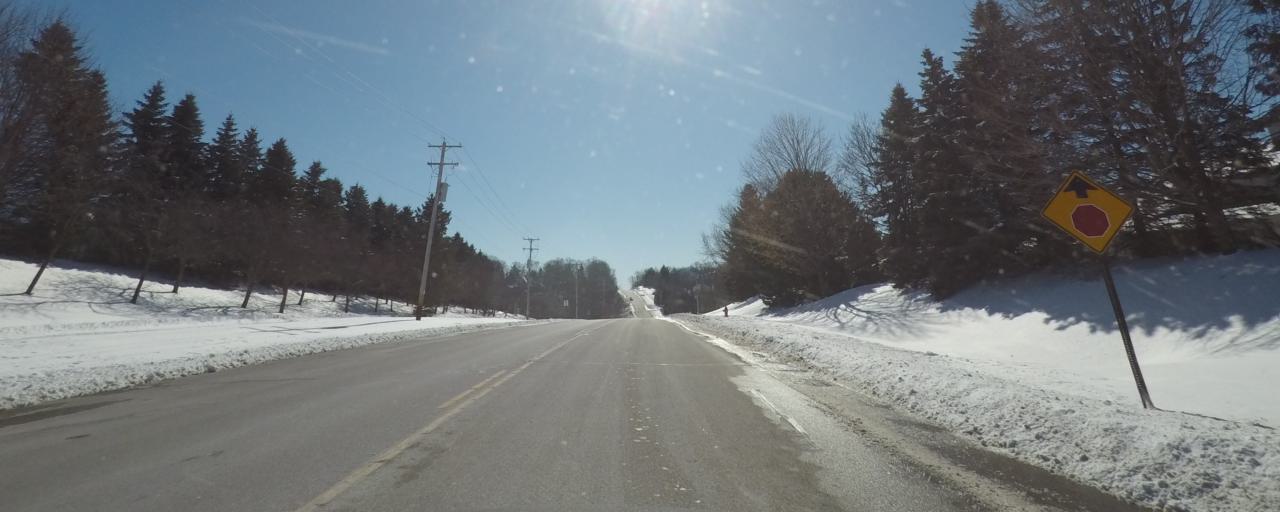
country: US
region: Wisconsin
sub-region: Waukesha County
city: Brookfield
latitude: 43.0258
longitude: -88.1468
